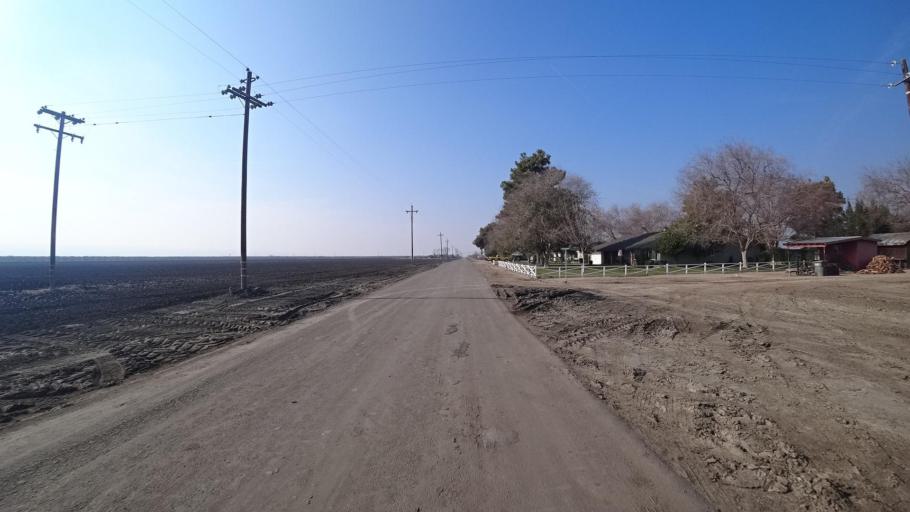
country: US
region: California
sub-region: Kern County
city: Buttonwillow
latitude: 35.3693
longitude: -119.4292
